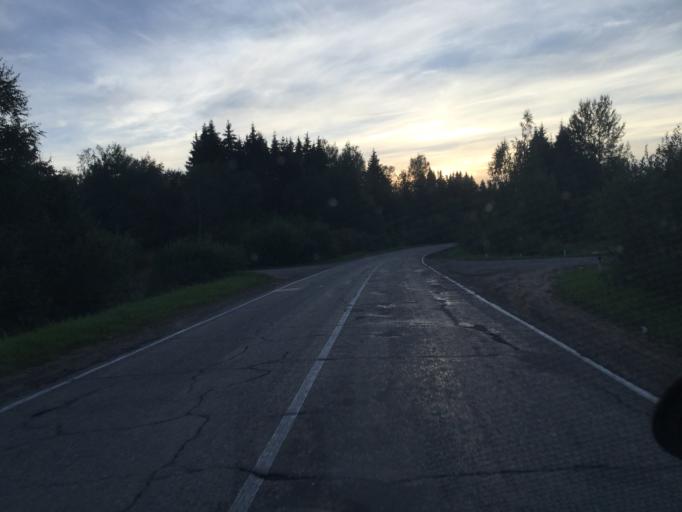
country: RU
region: Pskov
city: Nevel'
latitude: 55.9830
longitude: 30.0069
